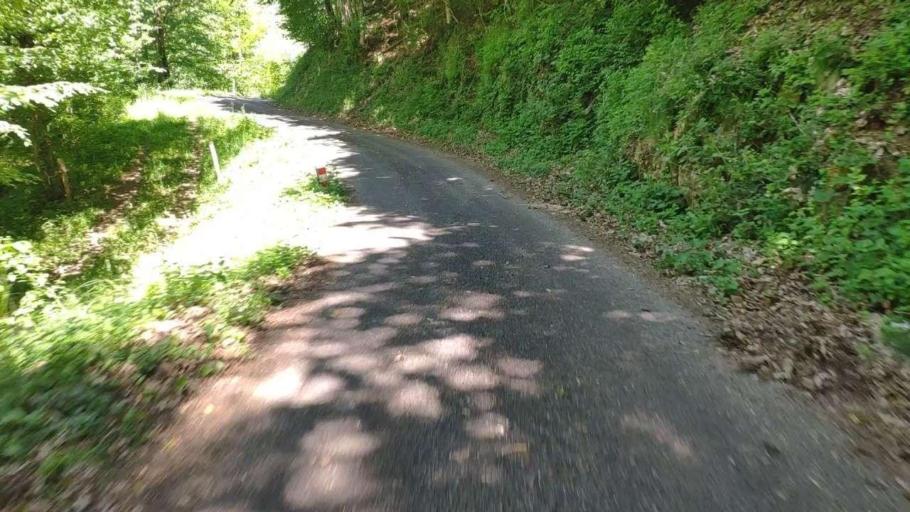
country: FR
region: Franche-Comte
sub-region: Departement du Jura
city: Poligny
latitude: 46.7521
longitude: 5.6763
